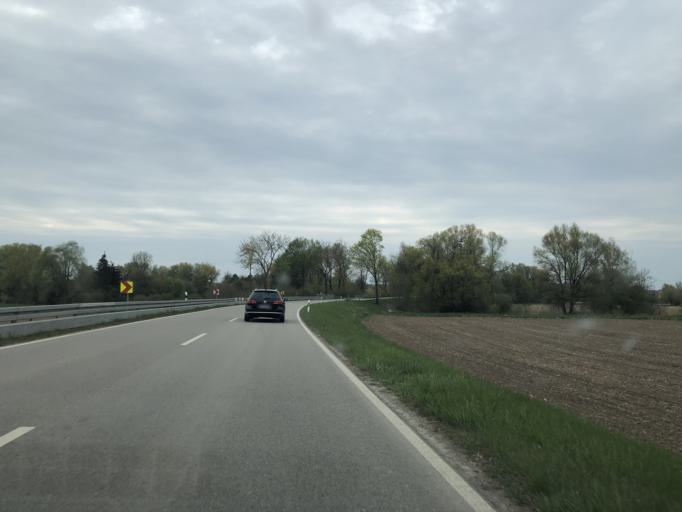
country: DE
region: Bavaria
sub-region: Upper Bavaria
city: Kirchdorf
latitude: 48.4462
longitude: 11.6610
